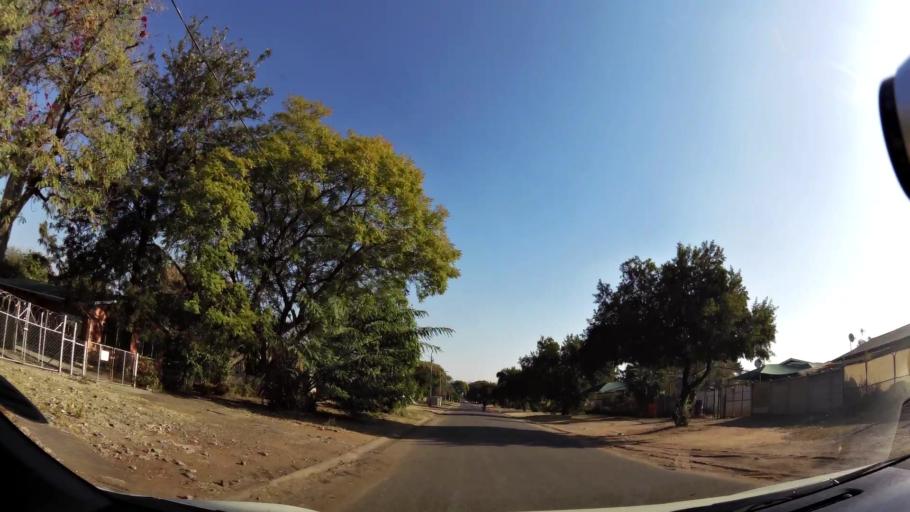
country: ZA
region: North-West
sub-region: Bojanala Platinum District Municipality
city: Rustenburg
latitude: -25.6592
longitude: 27.2620
